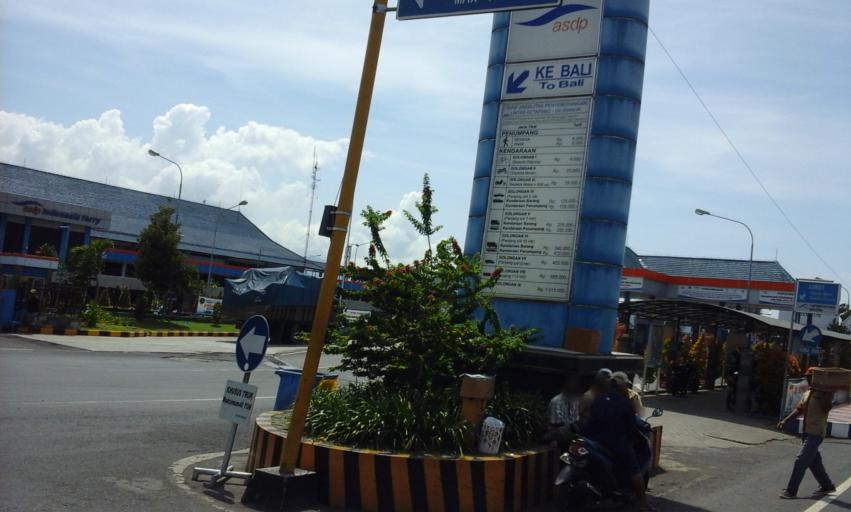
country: ID
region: East Java
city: Klatakan
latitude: -8.1423
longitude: 114.3994
